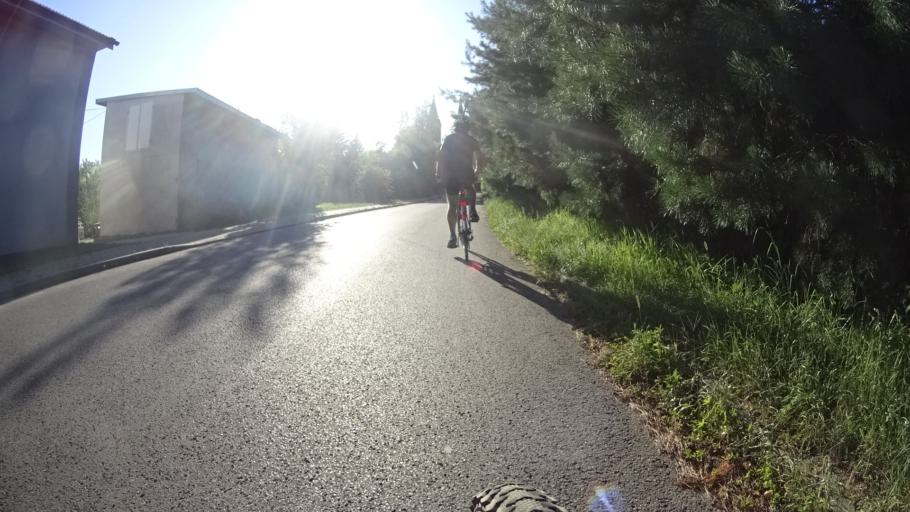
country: PL
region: Masovian Voivodeship
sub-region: Powiat bialobrzeski
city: Wysmierzyce
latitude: 51.6627
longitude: 20.8549
